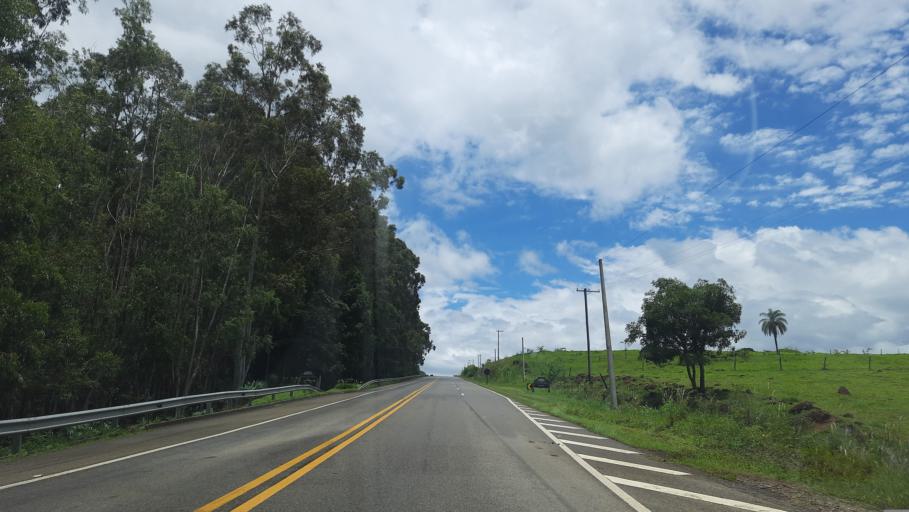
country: BR
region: Sao Paulo
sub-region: Vargem Grande Do Sul
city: Vargem Grande do Sul
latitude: -21.8014
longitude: -46.8028
